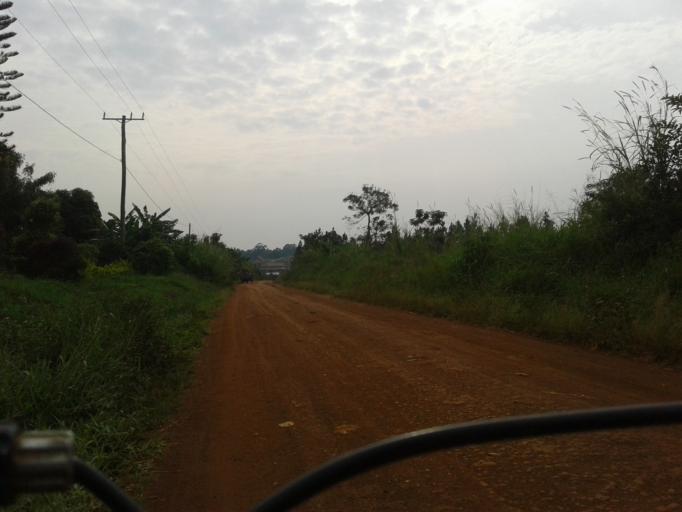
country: UG
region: Western Region
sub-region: Hoima District
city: Hoima
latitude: 1.4268
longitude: 31.3285
